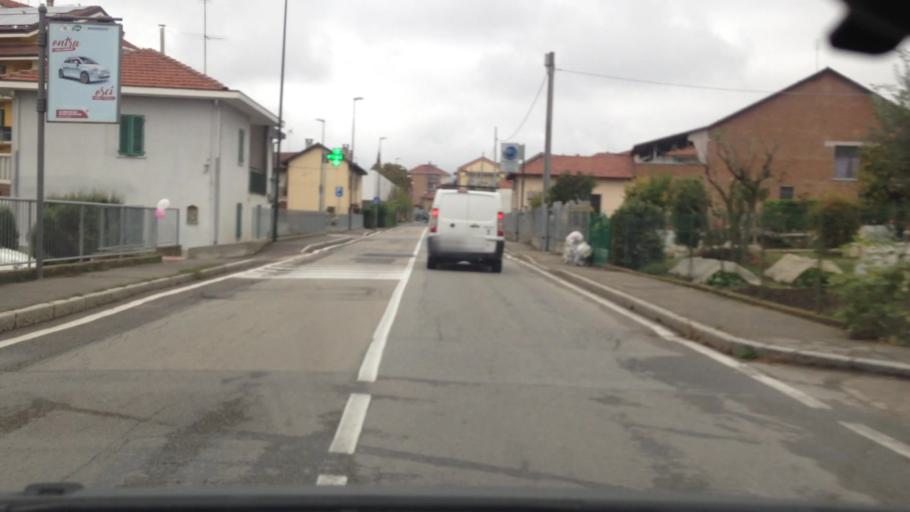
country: IT
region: Piedmont
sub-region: Provincia di Torino
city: Chieri
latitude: 45.0063
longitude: 7.8343
